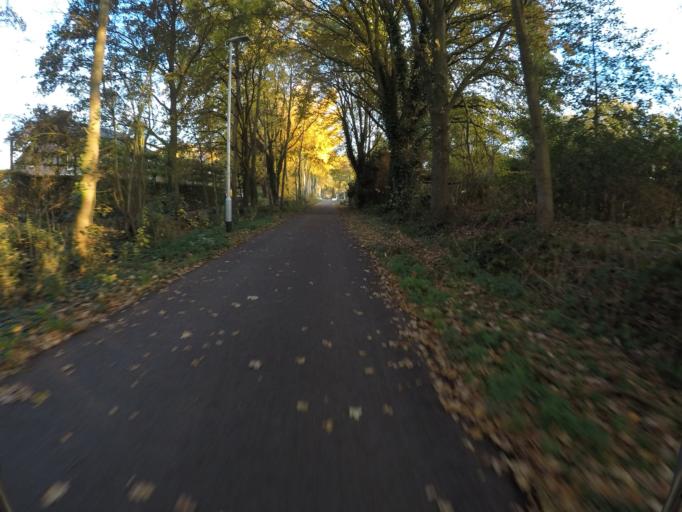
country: BE
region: Flanders
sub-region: Provincie Antwerpen
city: Hulshout
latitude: 51.0928
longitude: 4.8253
